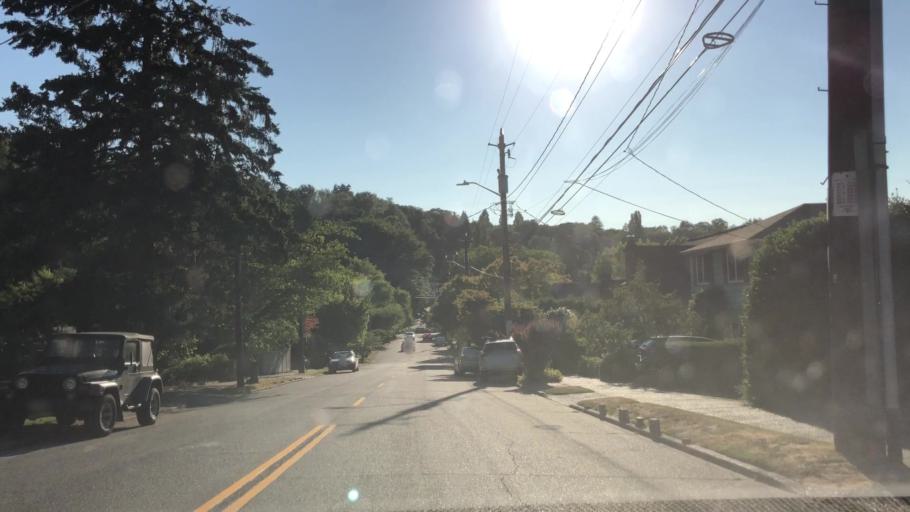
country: US
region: Washington
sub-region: King County
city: Seattle
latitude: 47.6396
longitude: -122.3076
